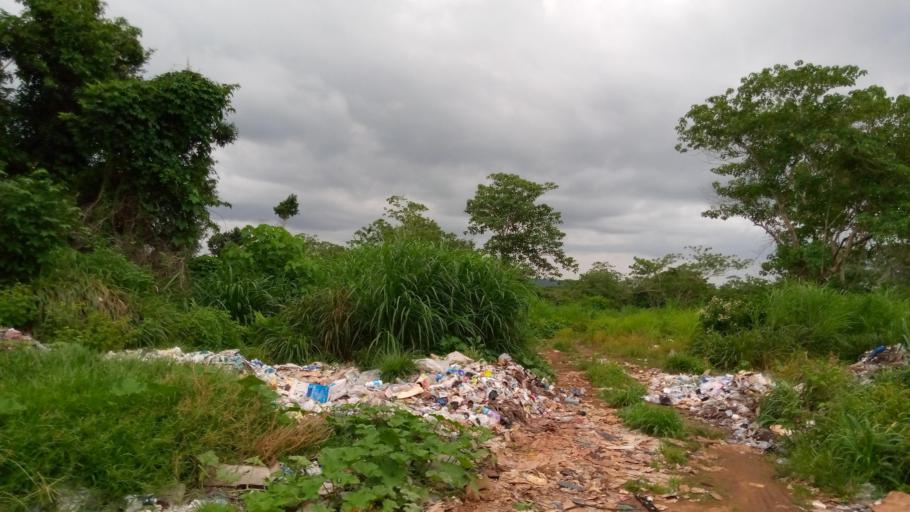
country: SL
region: Southern Province
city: Moyamba
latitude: 8.1662
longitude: -12.4668
